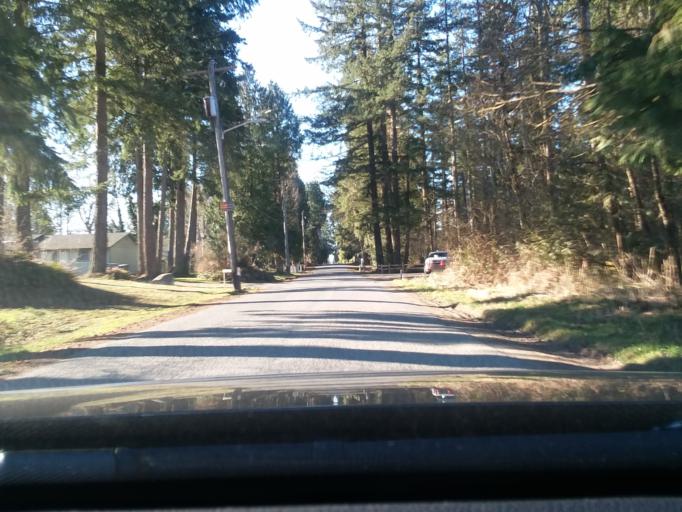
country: US
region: Washington
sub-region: Pierce County
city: Summit
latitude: 47.1364
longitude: -122.3628
